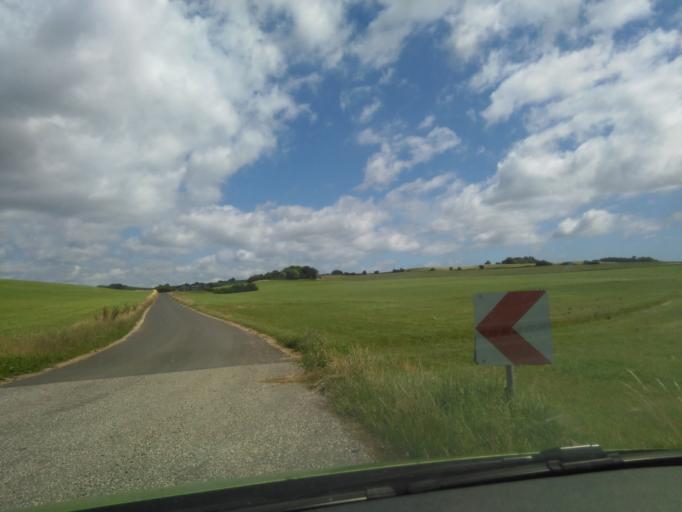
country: DK
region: Central Jutland
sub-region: Arhus Kommune
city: Logten
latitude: 56.1757
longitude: 10.3782
